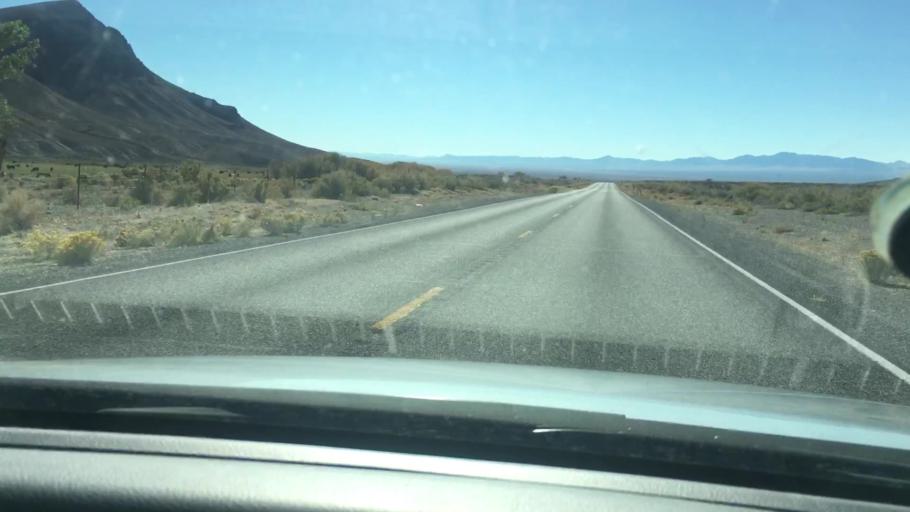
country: US
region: Nevada
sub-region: White Pine County
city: Ely
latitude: 38.7588
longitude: -115.4445
